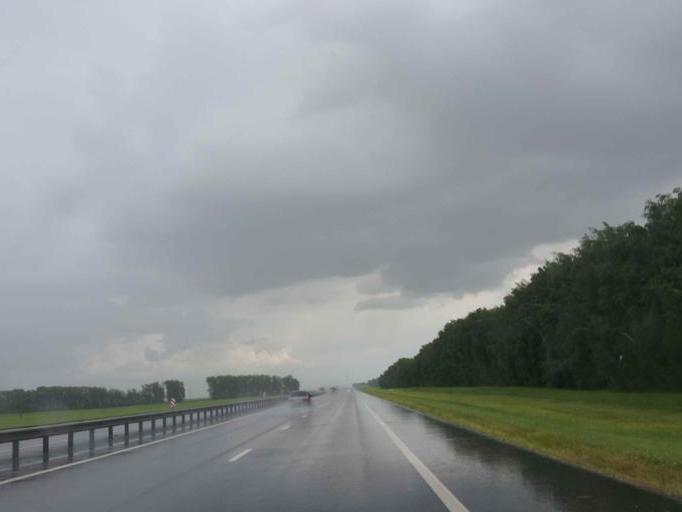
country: RU
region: Tambov
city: Zavoronezhskoye
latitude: 52.8337
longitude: 40.8745
